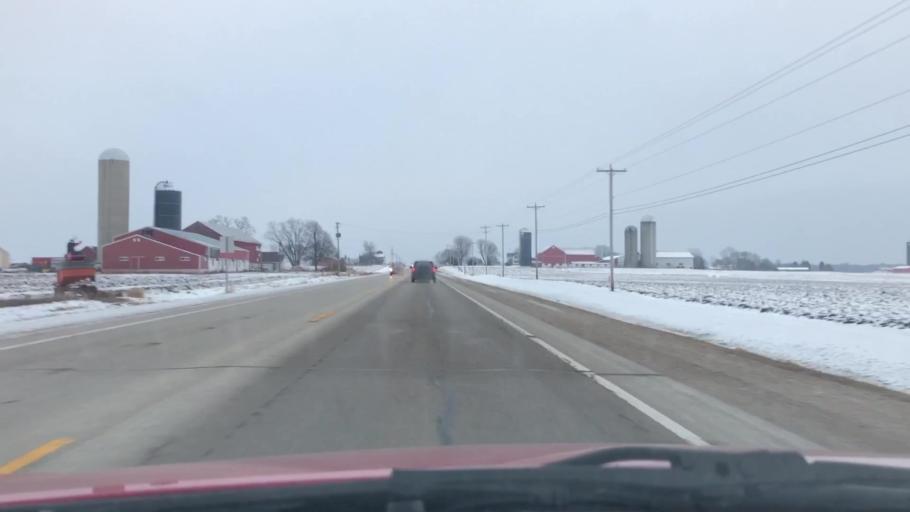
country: US
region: Wisconsin
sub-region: Outagamie County
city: Seymour
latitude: 44.5004
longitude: -88.3178
